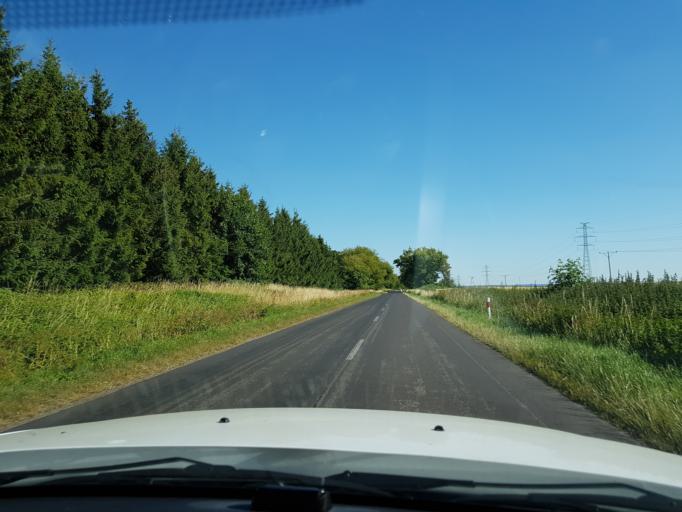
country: PL
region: West Pomeranian Voivodeship
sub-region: Powiat lobeski
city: Lobez
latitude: 53.6685
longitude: 15.6076
